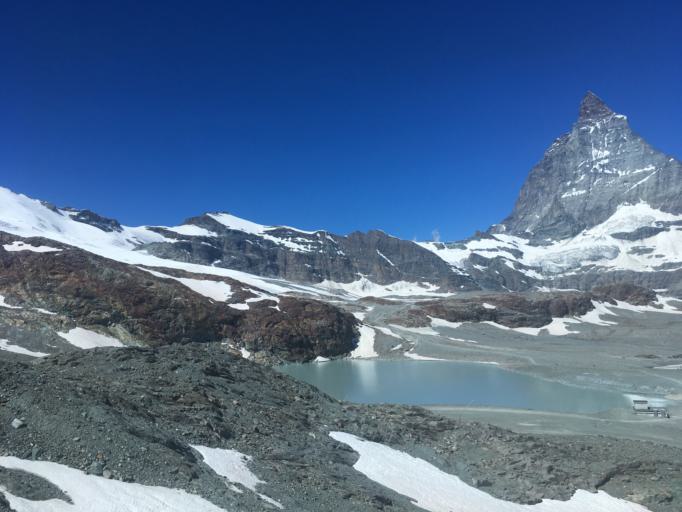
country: CH
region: Valais
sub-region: Visp District
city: Zermatt
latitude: 45.9728
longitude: 7.7208
